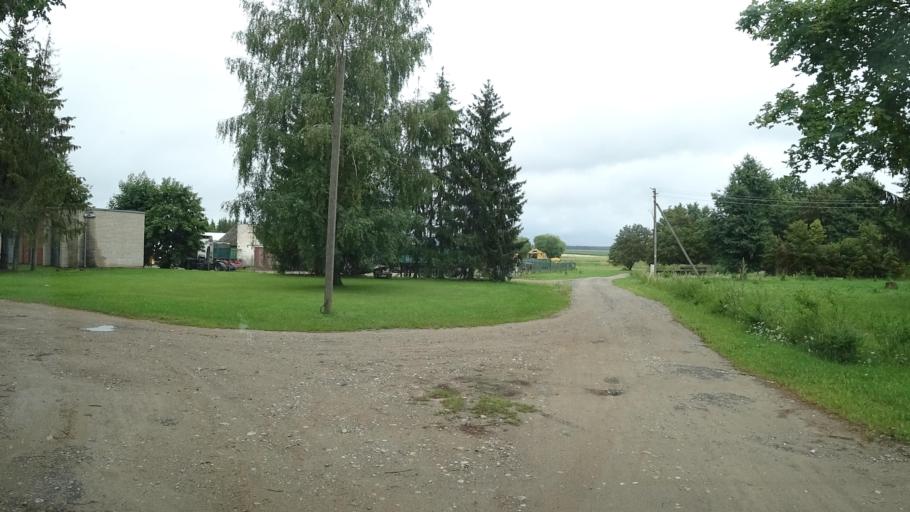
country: LT
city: Ramygala
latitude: 55.4201
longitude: 24.2389
